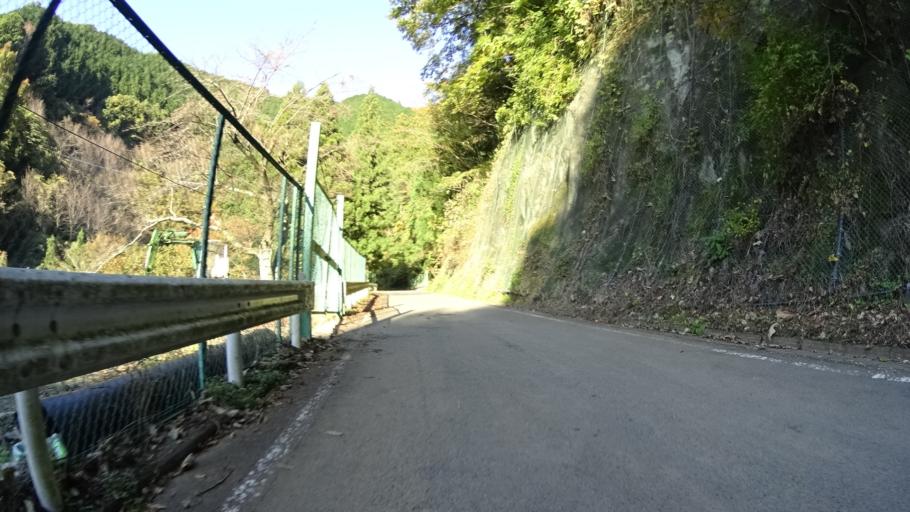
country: JP
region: Yamanashi
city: Uenohara
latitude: 35.6576
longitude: 139.1616
